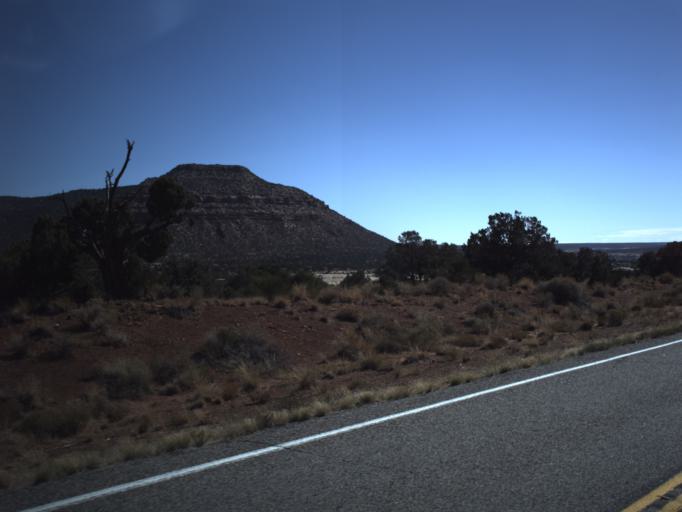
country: US
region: Utah
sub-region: San Juan County
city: Blanding
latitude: 37.6281
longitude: -110.0873
